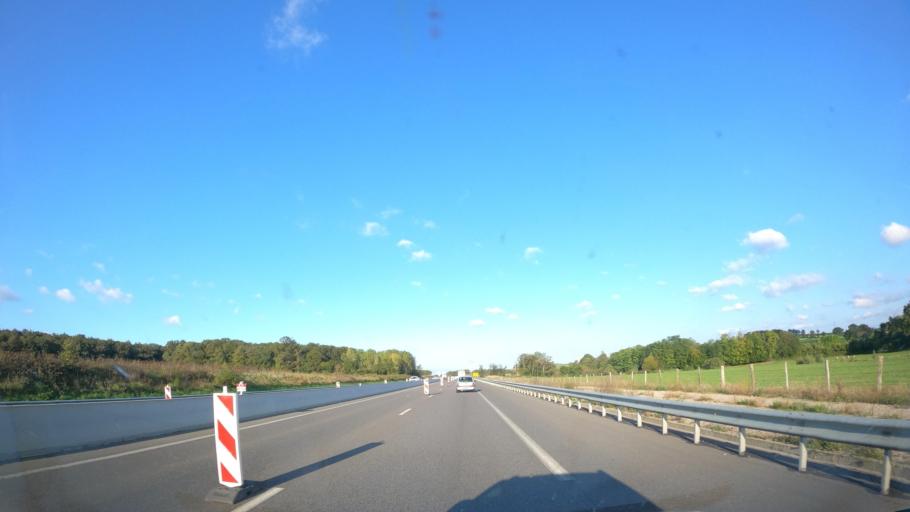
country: FR
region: Bourgogne
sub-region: Departement de Saone-et-Loire
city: Saint-Eusebe
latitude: 46.7089
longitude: 4.4250
